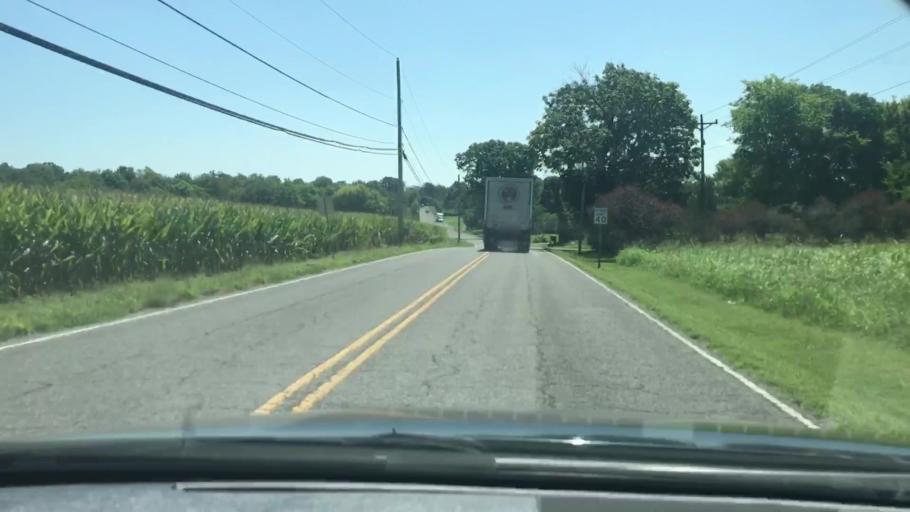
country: US
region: Tennessee
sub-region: Sumner County
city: Gallatin
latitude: 36.4029
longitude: -86.4909
